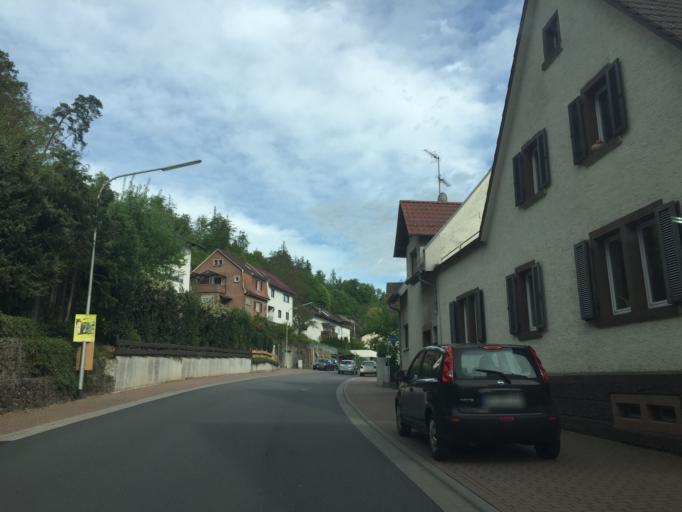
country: DE
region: Hesse
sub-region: Regierungsbezirk Darmstadt
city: Birkenau
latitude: 49.5387
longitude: 8.7120
